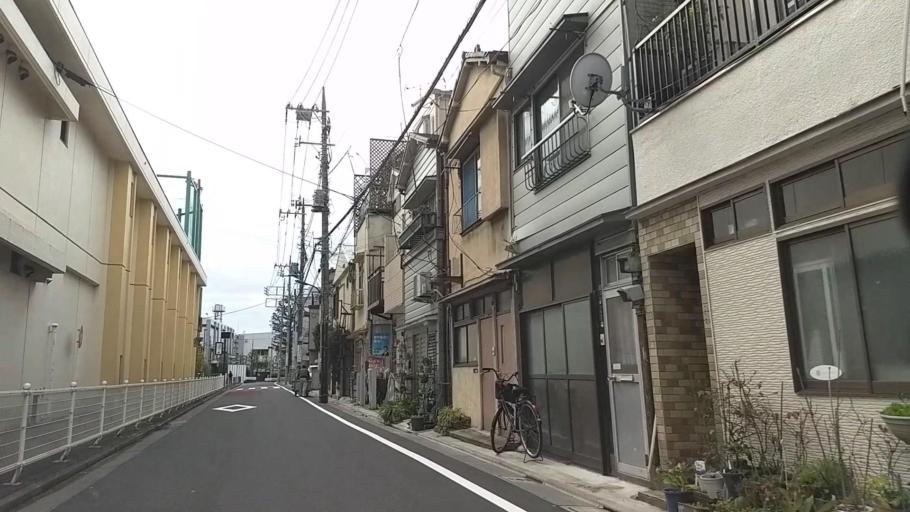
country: JP
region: Tokyo
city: Tokyo
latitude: 35.6111
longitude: 139.7203
